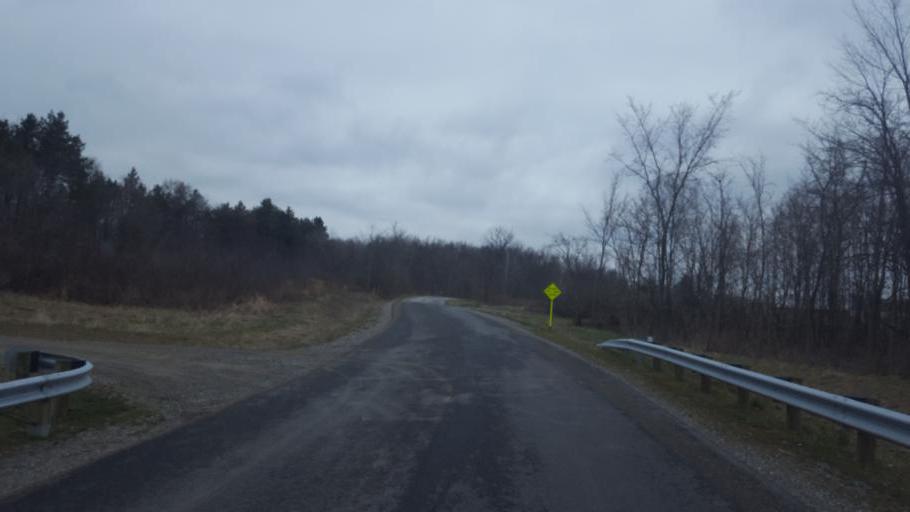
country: US
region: Ohio
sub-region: Delaware County
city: Ashley
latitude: 40.4251
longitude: -83.0100
